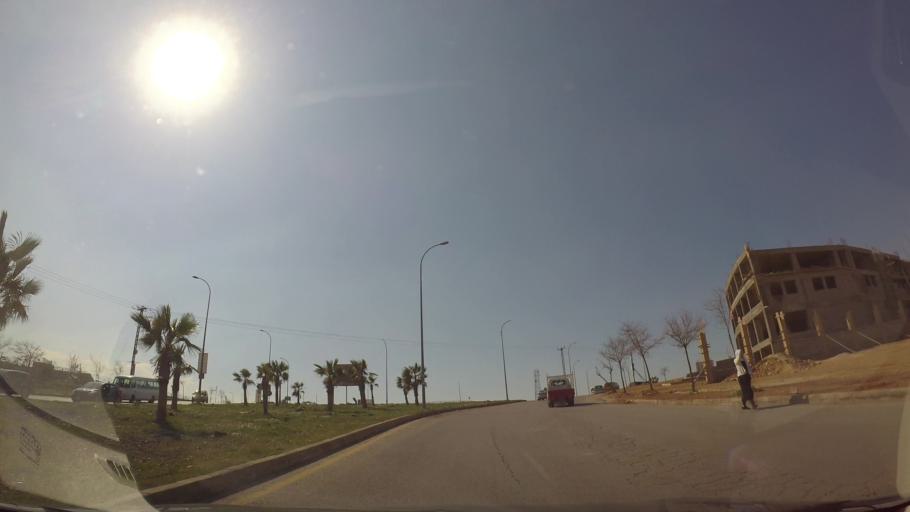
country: JO
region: Zarqa
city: Zarqa
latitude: 32.0664
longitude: 36.1025
